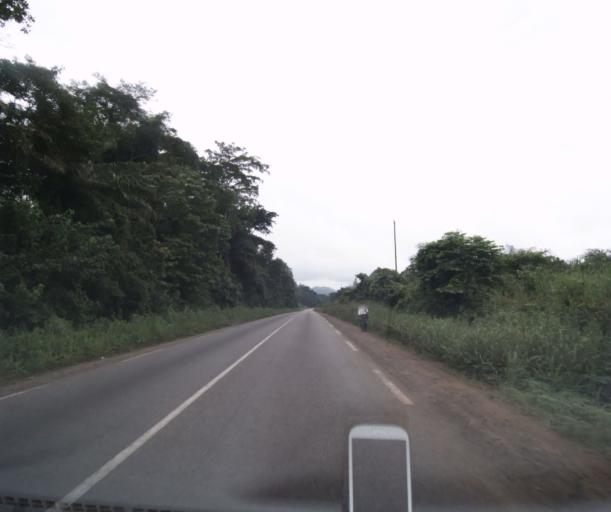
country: CM
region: Littoral
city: Edea
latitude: 3.8071
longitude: 10.2675
